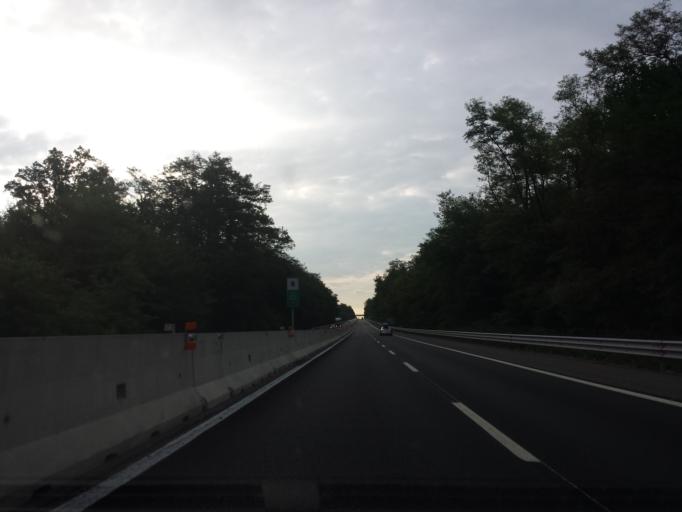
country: IT
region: Lombardy
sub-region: Provincia di Varese
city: Vergiate
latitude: 45.7124
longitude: 8.7149
